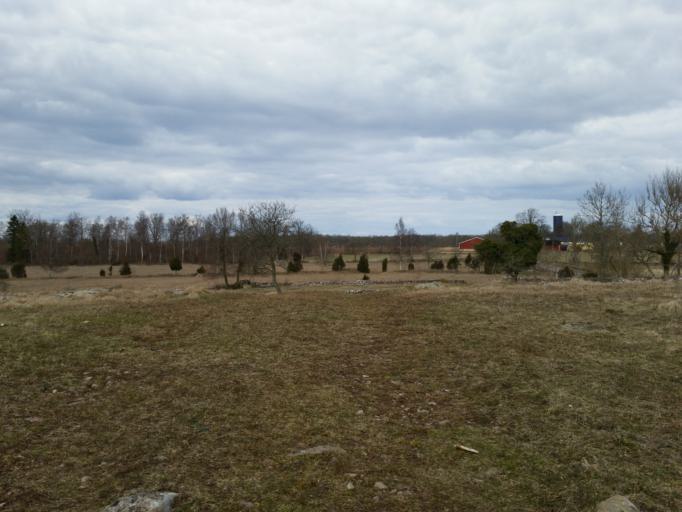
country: SE
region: Kalmar
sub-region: Morbylanga Kommun
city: Sodra Sandby
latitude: 56.6785
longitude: 16.5806
